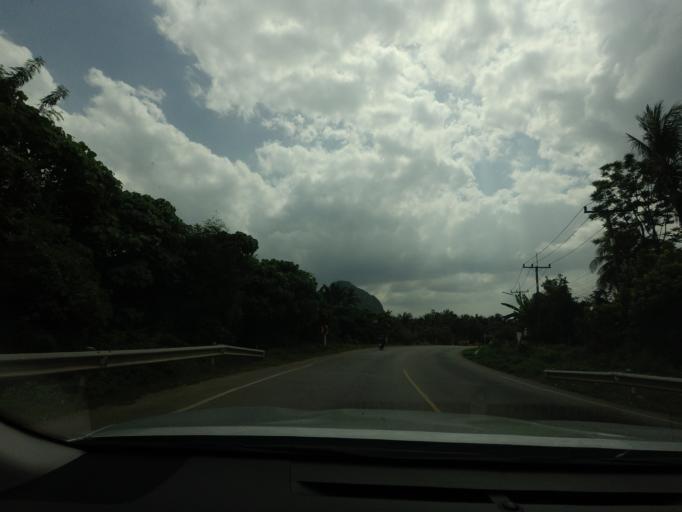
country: TH
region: Phangnga
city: Ban Ao Nang
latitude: 8.1162
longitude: 98.8021
